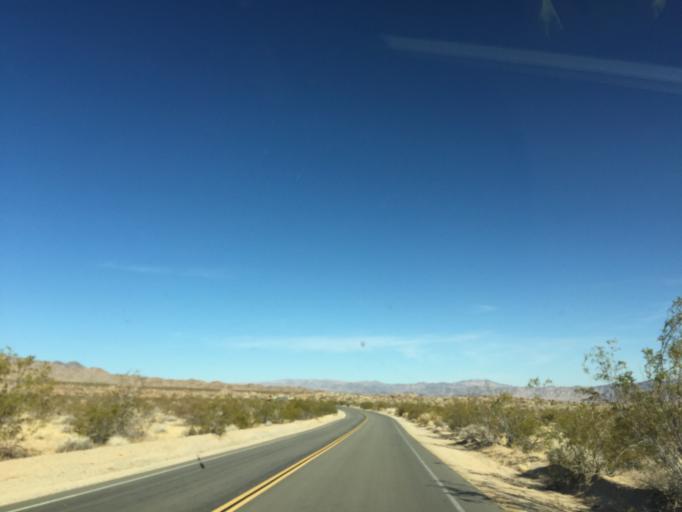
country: US
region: California
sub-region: San Bernardino County
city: Twentynine Palms
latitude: 33.8440
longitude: -115.7746
